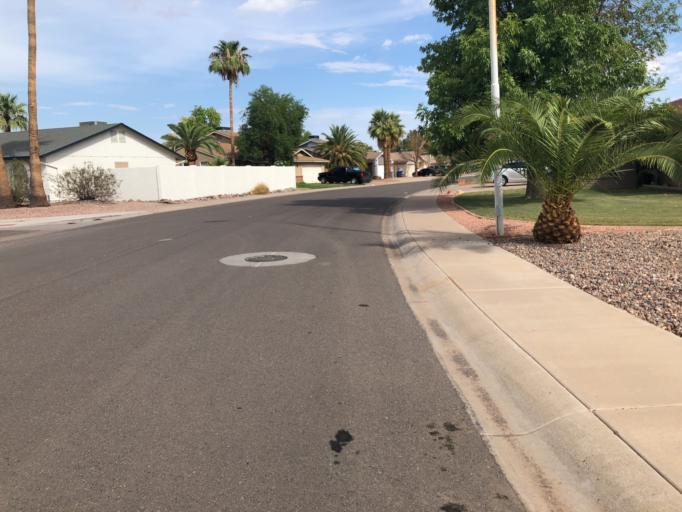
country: US
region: Arizona
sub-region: Maricopa County
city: San Carlos
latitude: 33.3559
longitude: -111.8720
